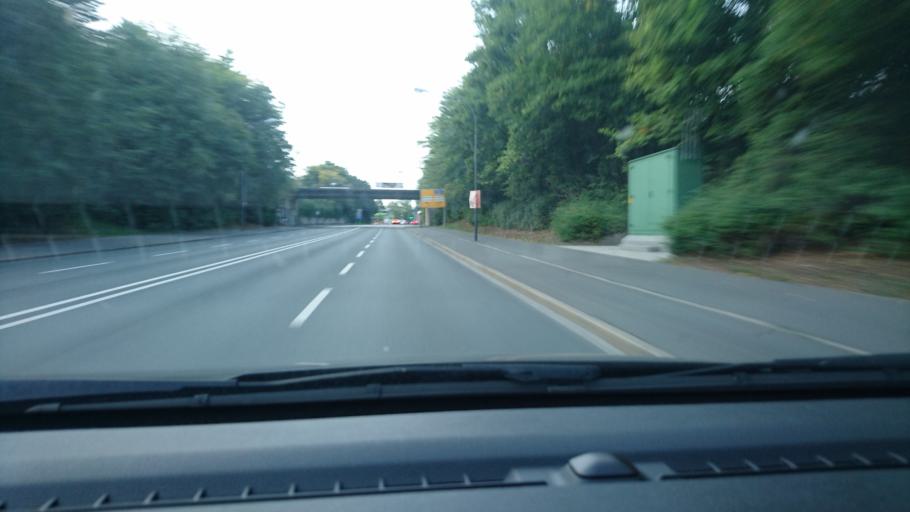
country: DE
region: Bavaria
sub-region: Upper Franconia
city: Bayreuth
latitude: 49.9523
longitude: 11.5985
